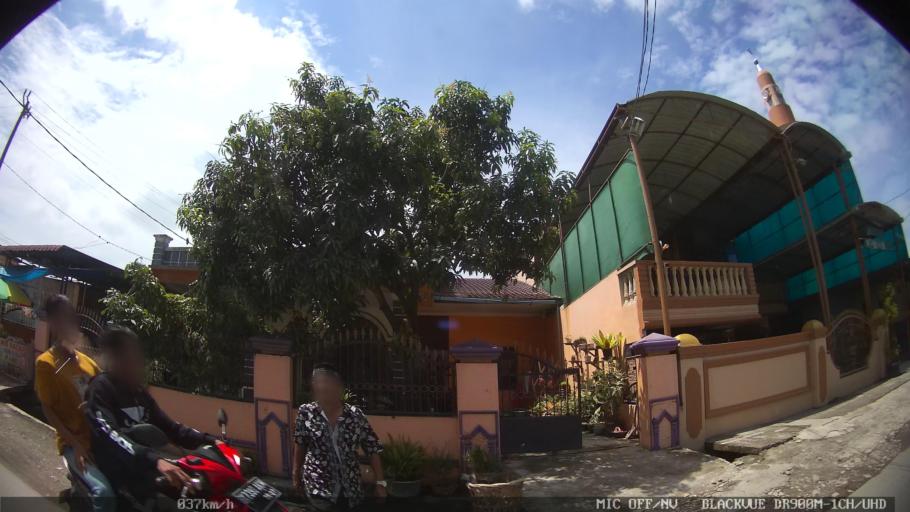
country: ID
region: North Sumatra
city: Percut
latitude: 3.6020
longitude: 98.7696
